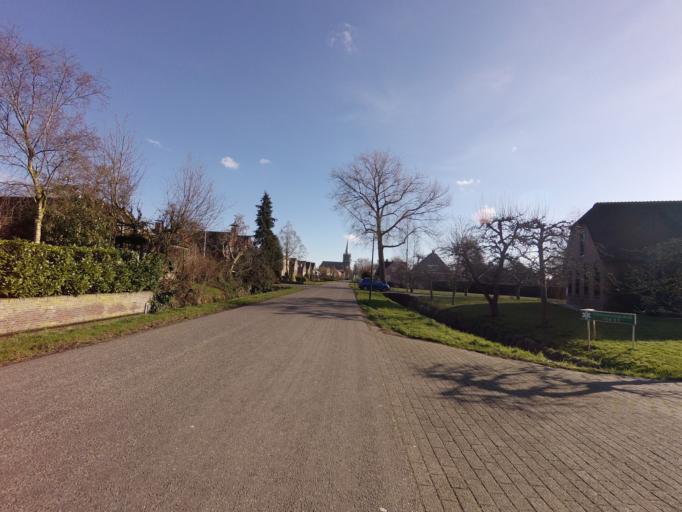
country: NL
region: Utrecht
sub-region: Gemeente IJsselstein
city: IJsselstein
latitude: 52.0220
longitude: 5.0352
